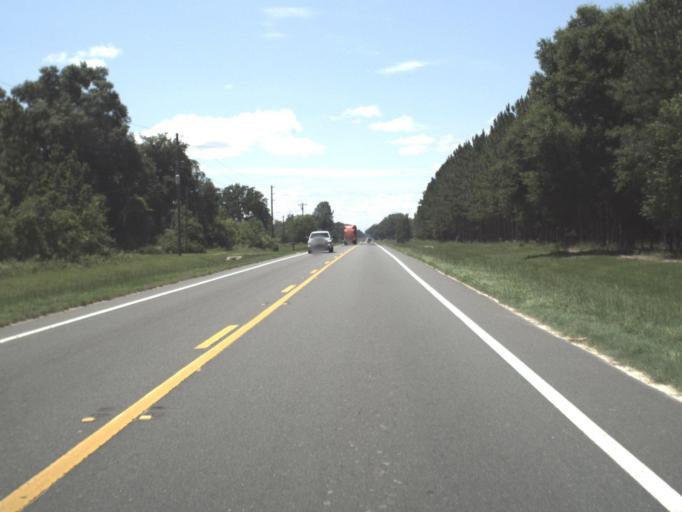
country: US
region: Florida
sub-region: Lafayette County
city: Mayo
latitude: 30.0936
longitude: -83.2323
